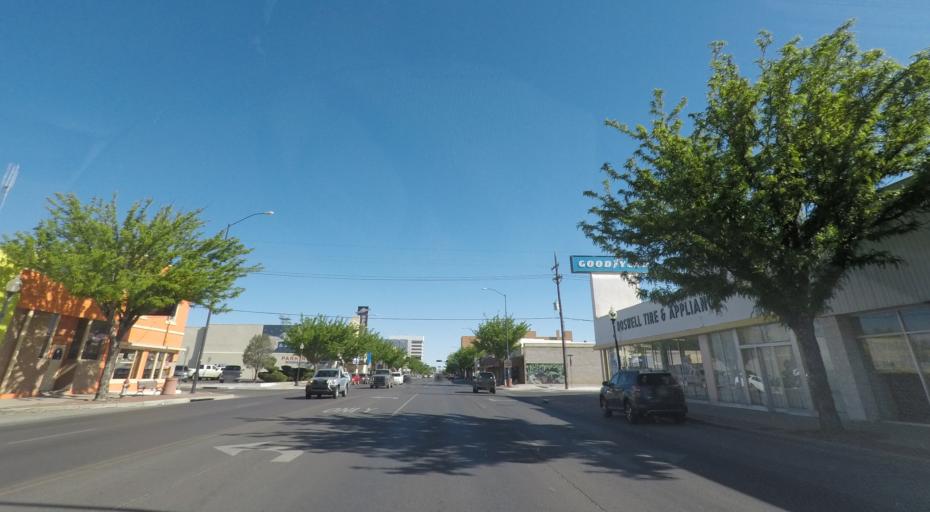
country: US
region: New Mexico
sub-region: Chaves County
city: Roswell
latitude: 33.3927
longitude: -104.5227
